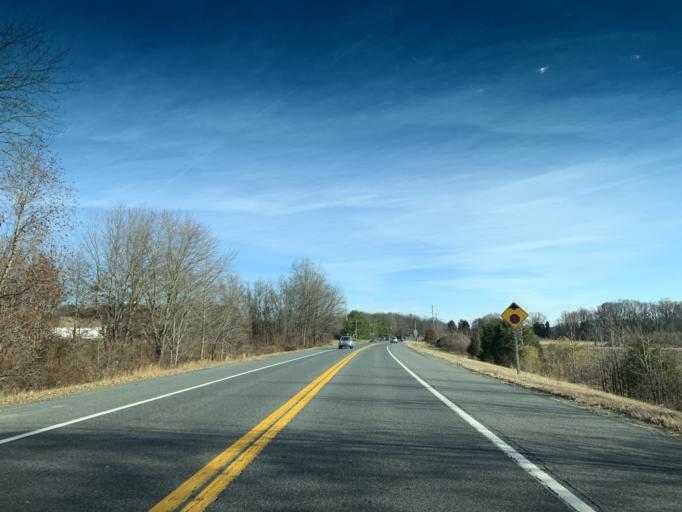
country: US
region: Maryland
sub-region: Harford County
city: Aberdeen
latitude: 39.5775
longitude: -76.1892
